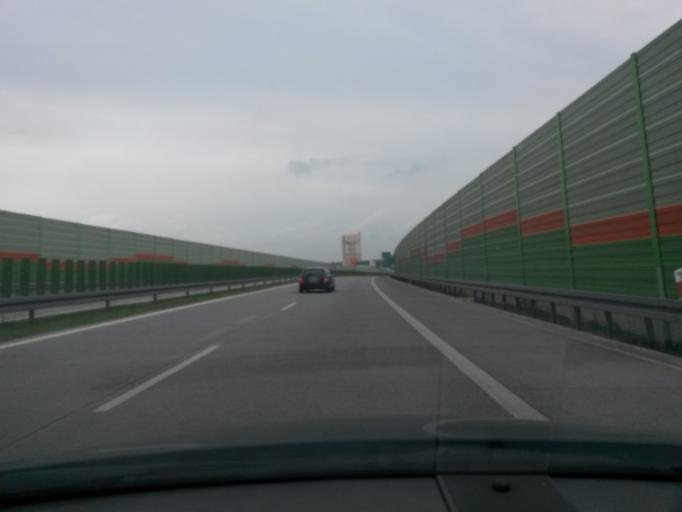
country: PL
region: Lodz Voivodeship
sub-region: Powiat rawski
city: Rawa Mazowiecka
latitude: 51.7678
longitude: 20.2717
